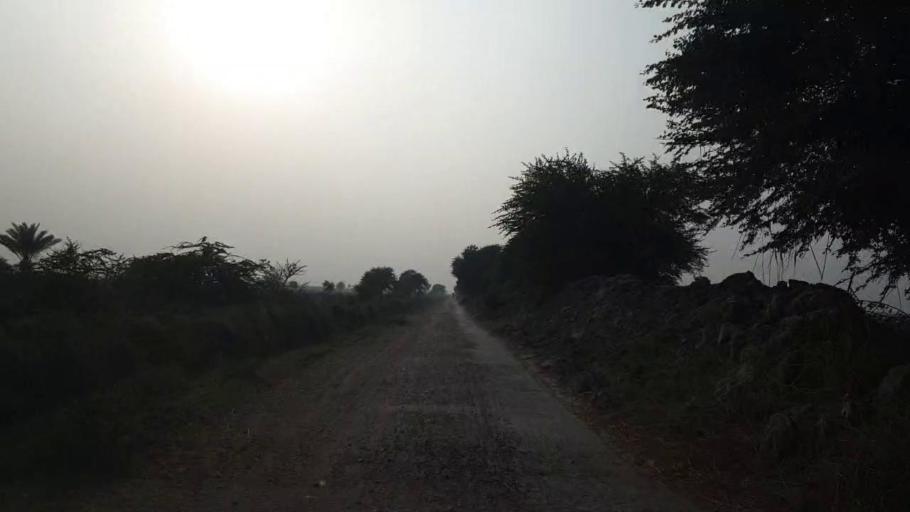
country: PK
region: Sindh
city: Mirpur Batoro
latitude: 24.6545
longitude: 68.3865
